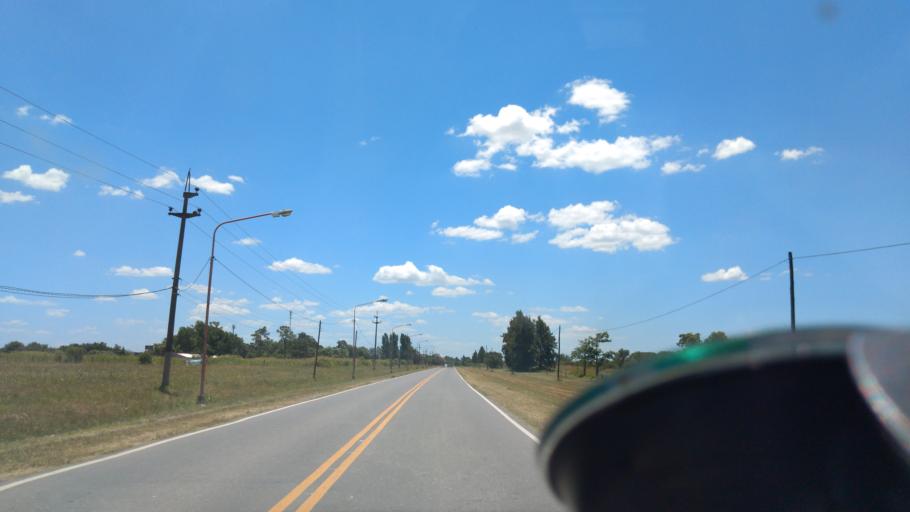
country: AR
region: Santa Fe
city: Laguna Paiva
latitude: -31.3261
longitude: -60.6591
